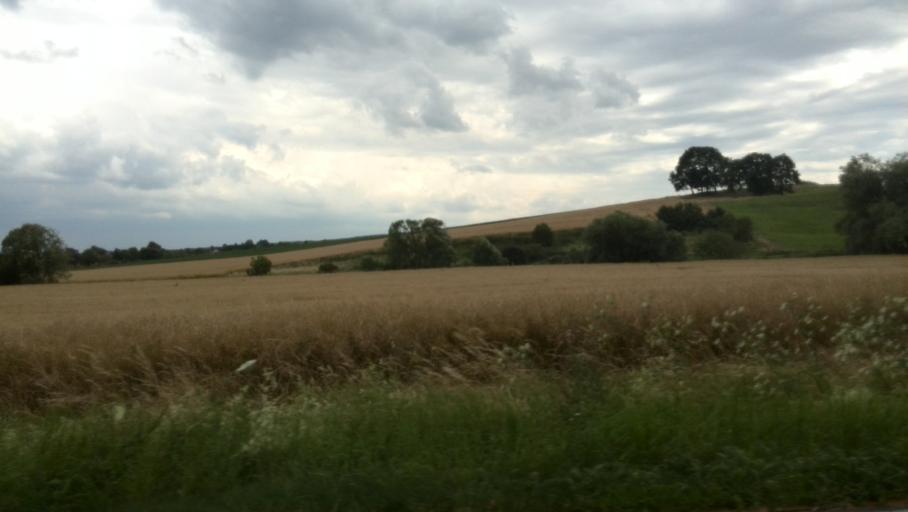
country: DE
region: Lower Saxony
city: Holle
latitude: 52.0805
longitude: 10.1705
